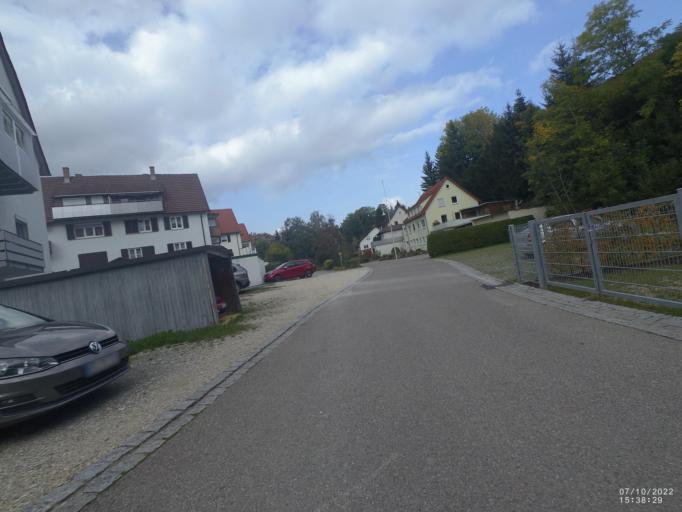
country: DE
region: Baden-Wuerttemberg
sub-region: Regierungsbezirk Stuttgart
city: Eislingen
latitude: 48.7068
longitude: 9.7111
